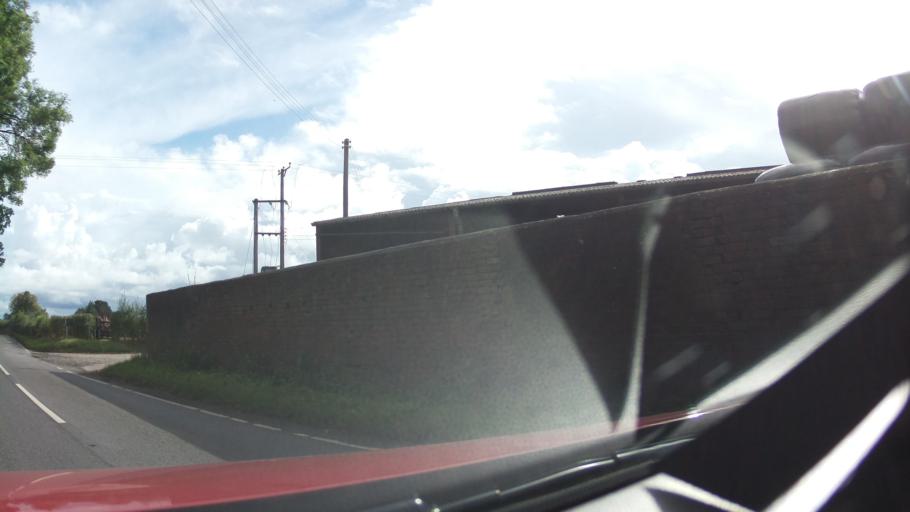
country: GB
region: England
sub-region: Telford and Wrekin
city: Madeley
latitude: 52.6264
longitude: -2.4132
